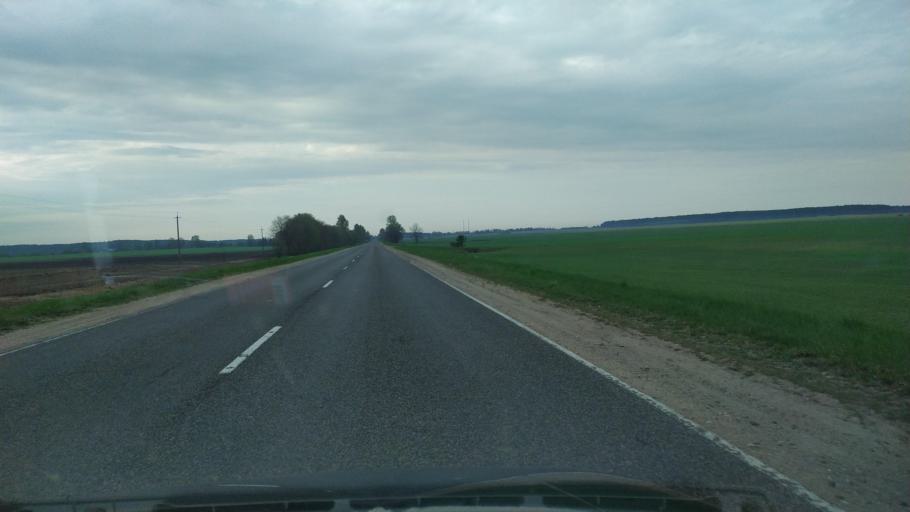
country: BY
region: Brest
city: Kamyanyets
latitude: 52.3669
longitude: 23.8867
